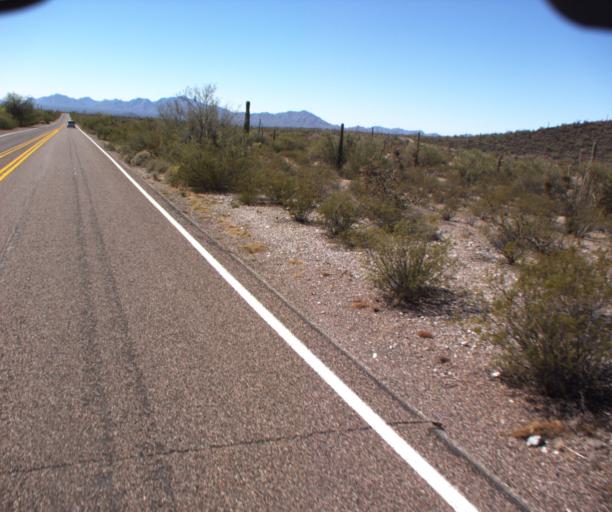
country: MX
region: Sonora
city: Sonoyta
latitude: 31.9491
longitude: -112.7995
